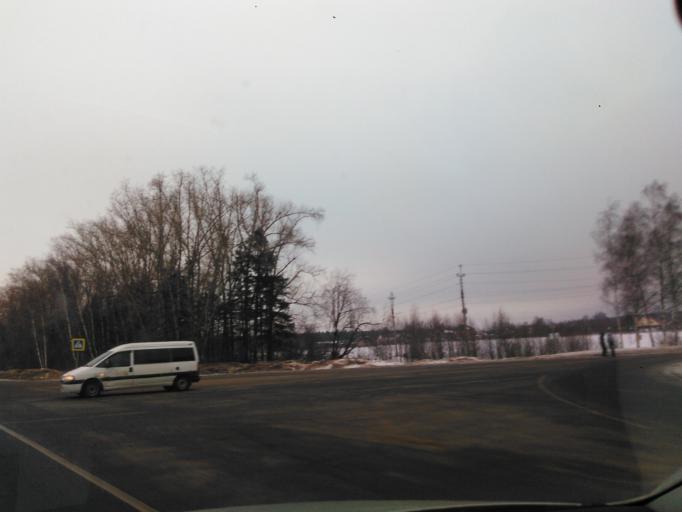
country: RU
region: Moskovskaya
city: Yermolino
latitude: 56.1357
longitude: 37.4137
